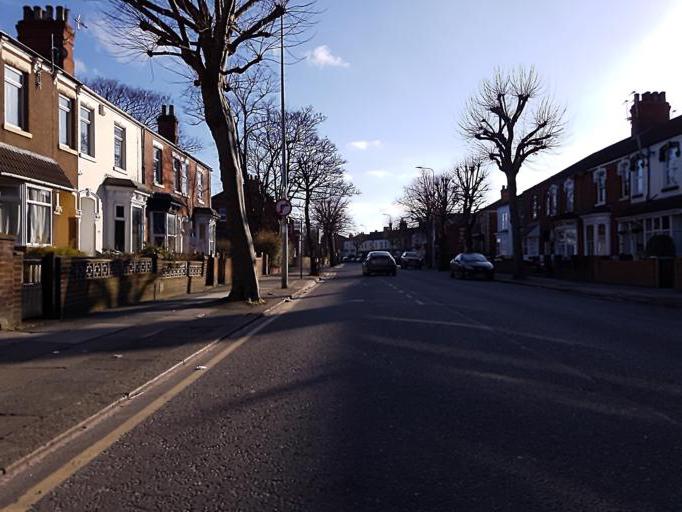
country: GB
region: England
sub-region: North East Lincolnshire
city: Grimsby
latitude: 53.5610
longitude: -0.0764
